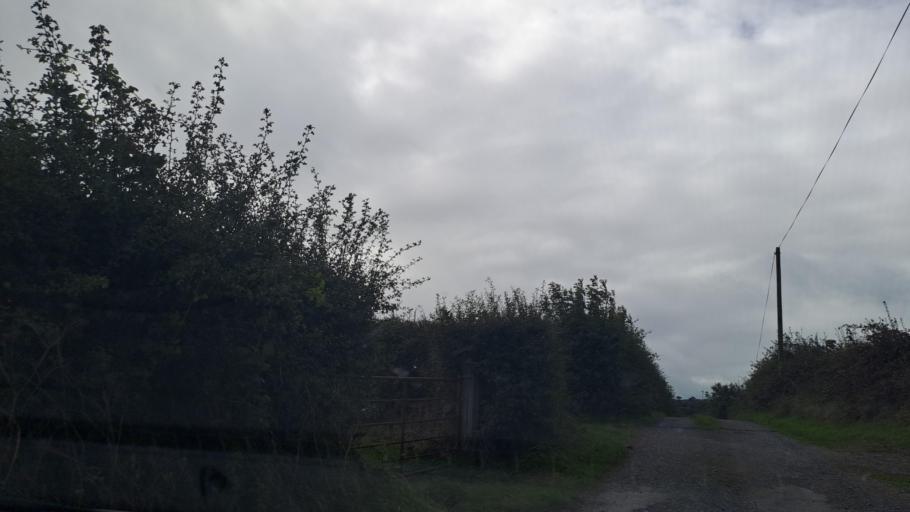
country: IE
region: Ulster
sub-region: An Cabhan
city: Kingscourt
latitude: 53.9772
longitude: -6.8433
